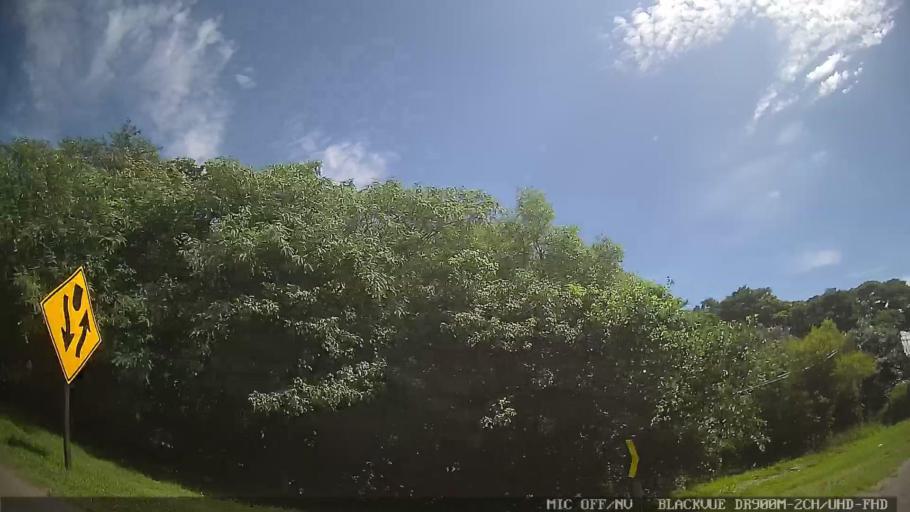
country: BR
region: Sao Paulo
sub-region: Tiete
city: Tiete
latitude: -23.1330
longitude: -47.6887
